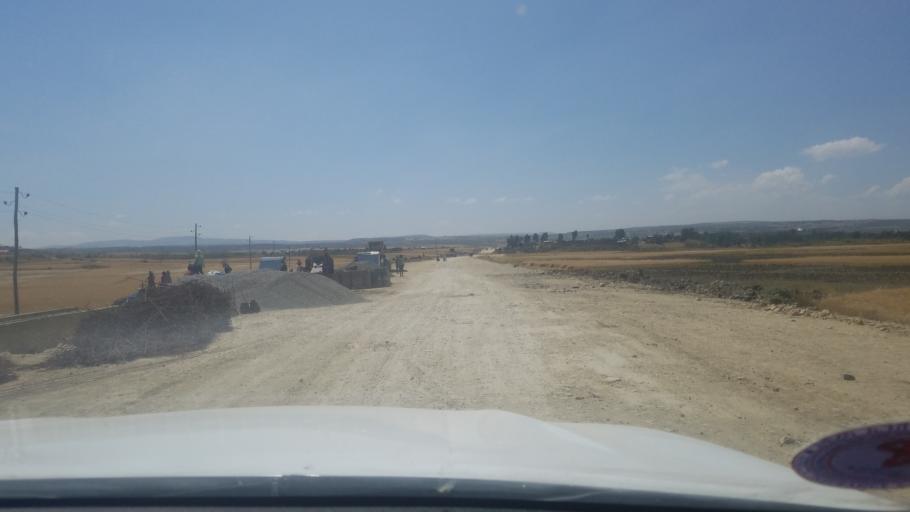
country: ET
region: Tigray
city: Mekele
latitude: 13.7677
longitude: 39.5913
